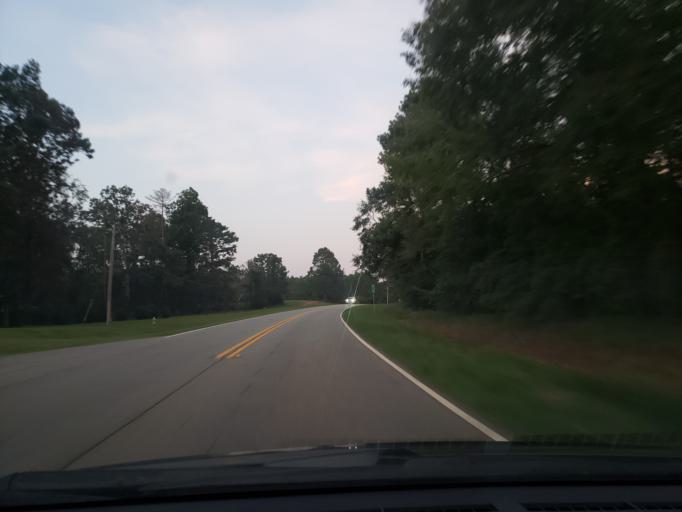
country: US
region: Georgia
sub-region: Dougherty County
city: Albany
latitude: 31.5852
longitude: -84.2925
